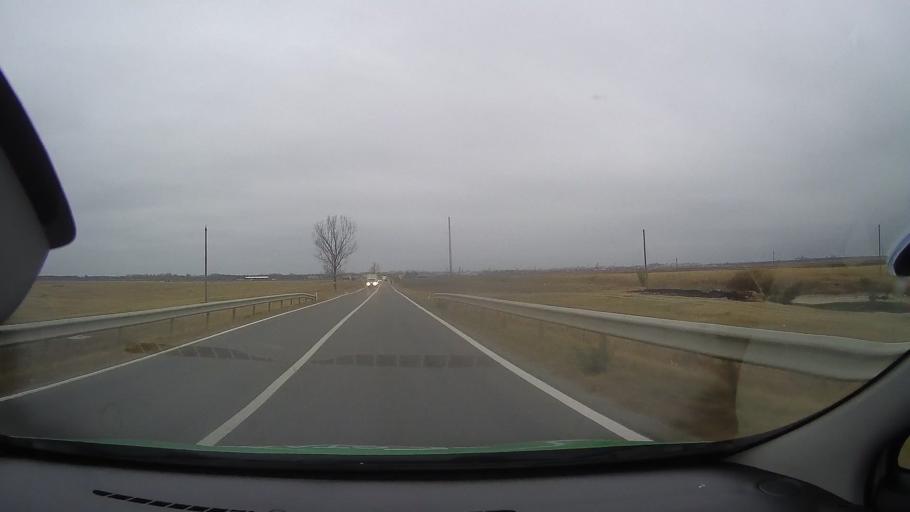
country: RO
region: Ialomita
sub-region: Comuna Slobozia
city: Slobozia
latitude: 44.5901
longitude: 27.3902
